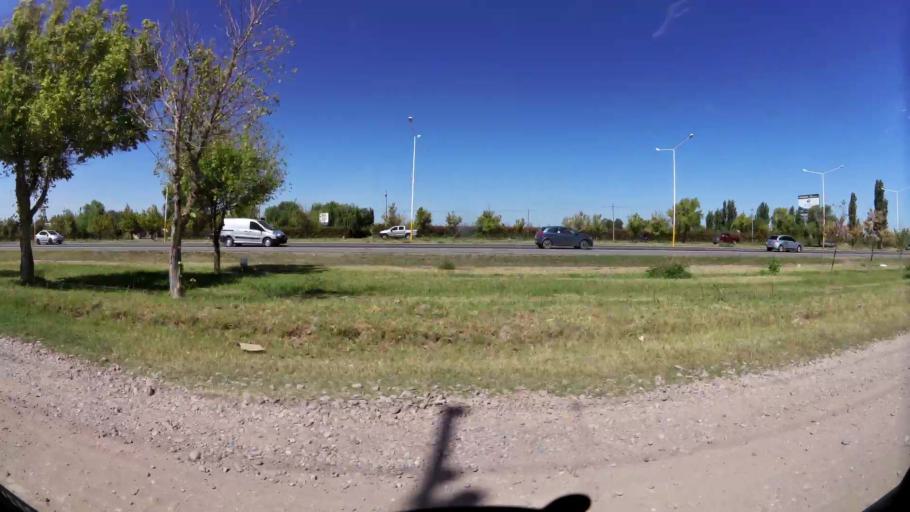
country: AR
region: Mendoza
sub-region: Departamento de Godoy Cruz
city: Godoy Cruz
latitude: -32.9802
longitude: -68.8484
